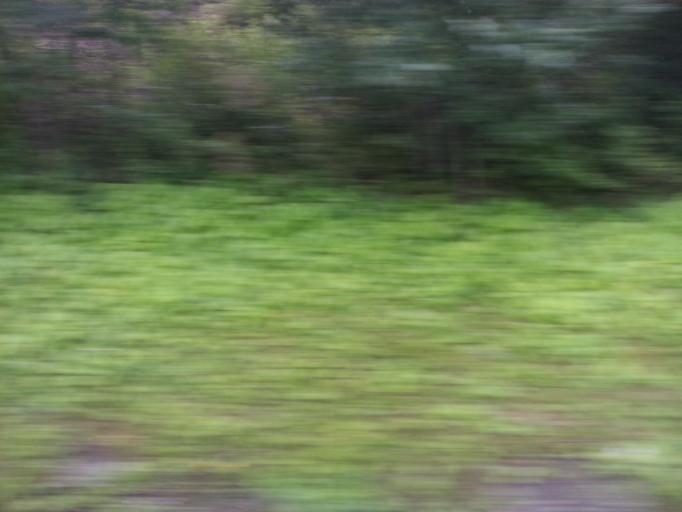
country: NO
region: Sor-Trondelag
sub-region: Malvik
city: Malvik
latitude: 63.4253
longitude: 10.5692
